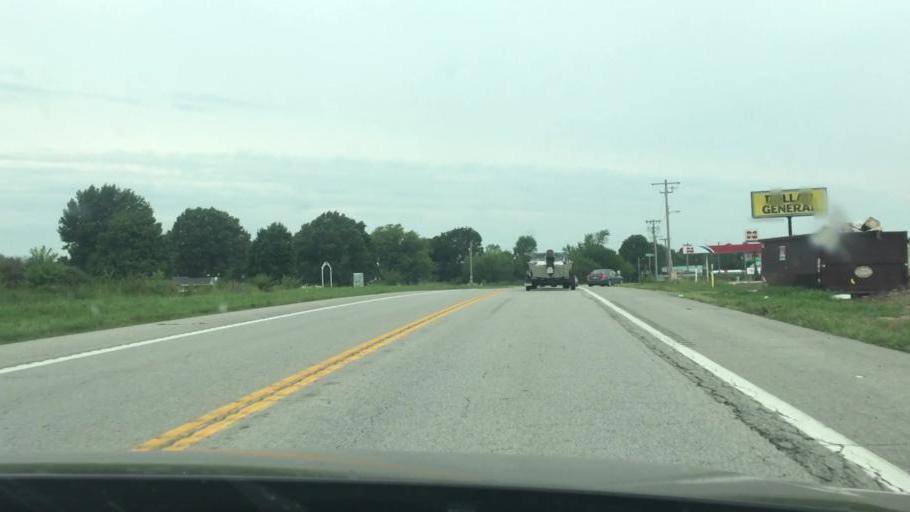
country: US
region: Missouri
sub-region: Pettis County
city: Sedalia
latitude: 38.6963
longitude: -93.1791
